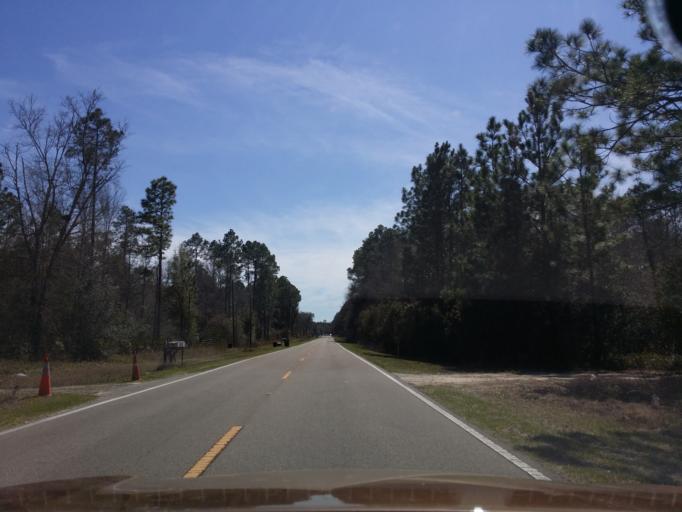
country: US
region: Florida
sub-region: Leon County
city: Woodville
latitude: 30.2991
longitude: -84.1584
